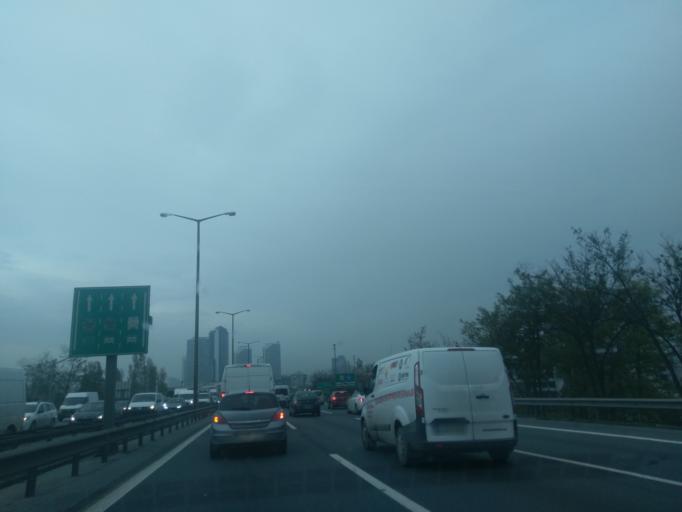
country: TR
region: Istanbul
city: Basaksehir
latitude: 41.0640
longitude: 28.7933
